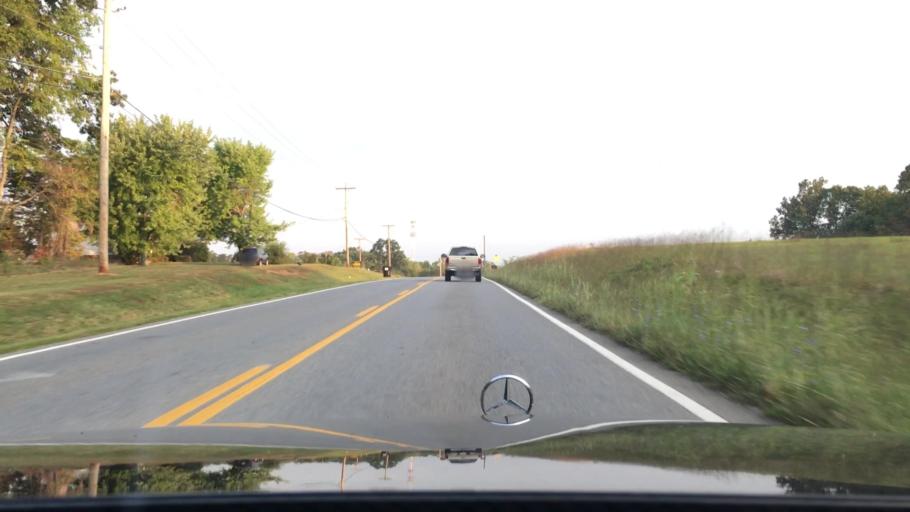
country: US
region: Virginia
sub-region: Campbell County
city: Timberlake
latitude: 37.3085
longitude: -79.2172
